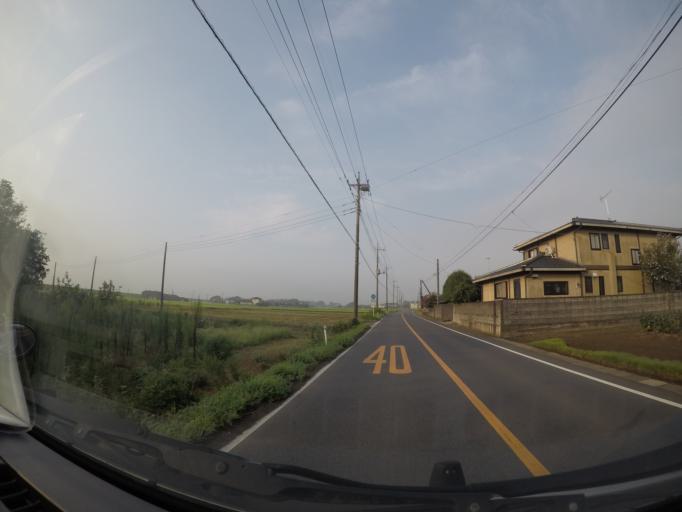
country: JP
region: Tochigi
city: Fujioka
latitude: 36.2740
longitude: 139.6784
